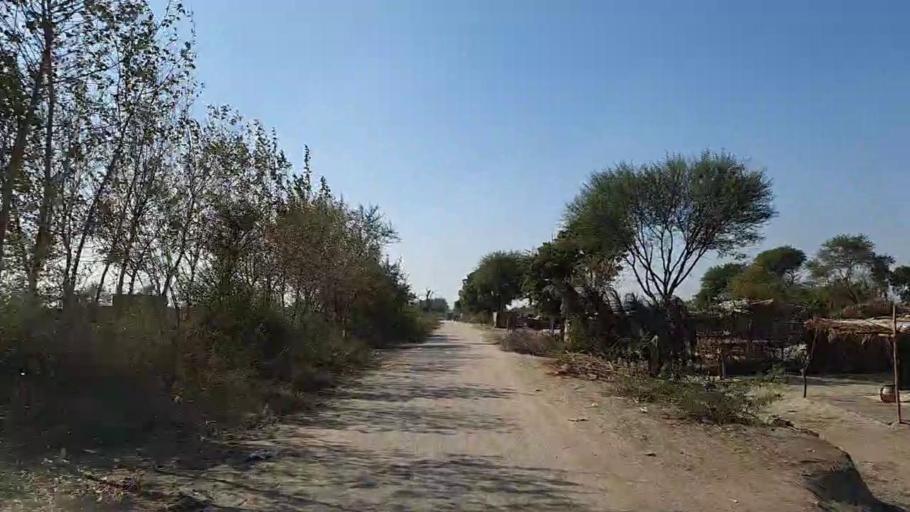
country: PK
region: Sindh
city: Nawabshah
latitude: 26.2447
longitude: 68.4374
